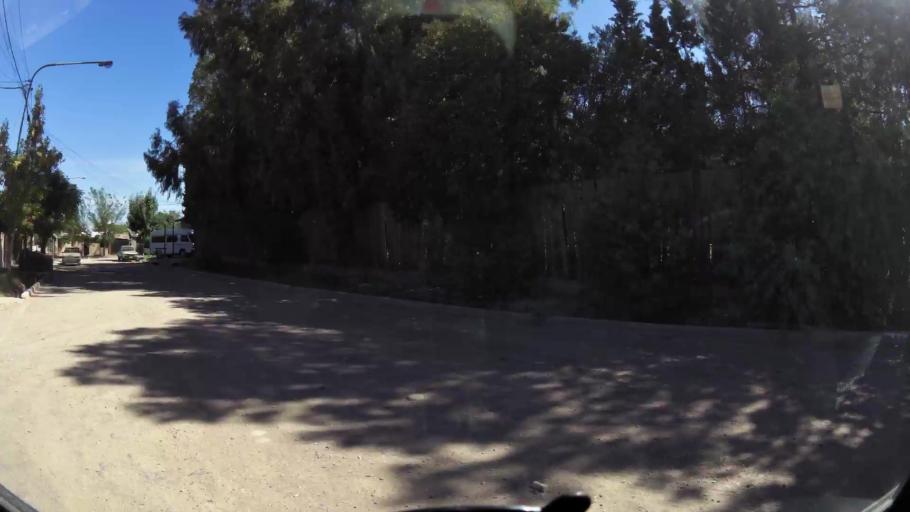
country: AR
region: Mendoza
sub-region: Departamento de Godoy Cruz
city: Godoy Cruz
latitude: -32.9628
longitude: -68.8365
